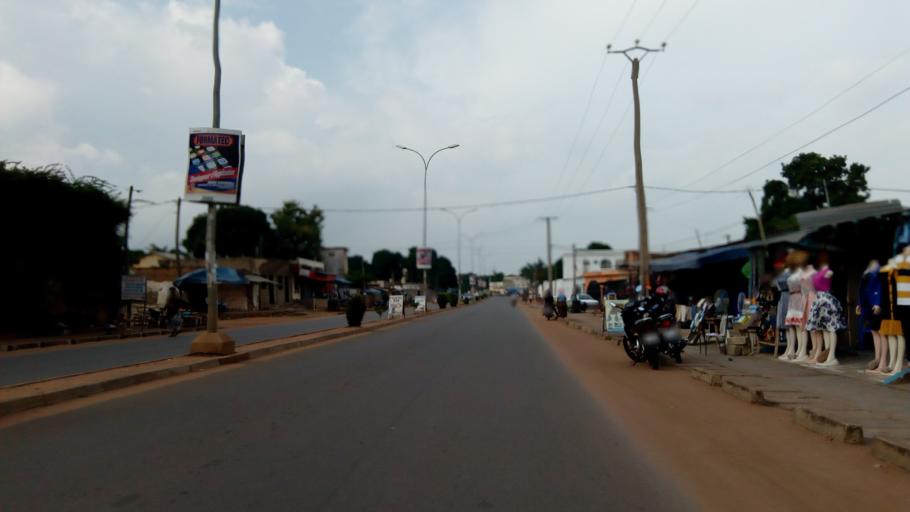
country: TG
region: Maritime
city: Lome
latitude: 6.2118
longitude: 1.1999
